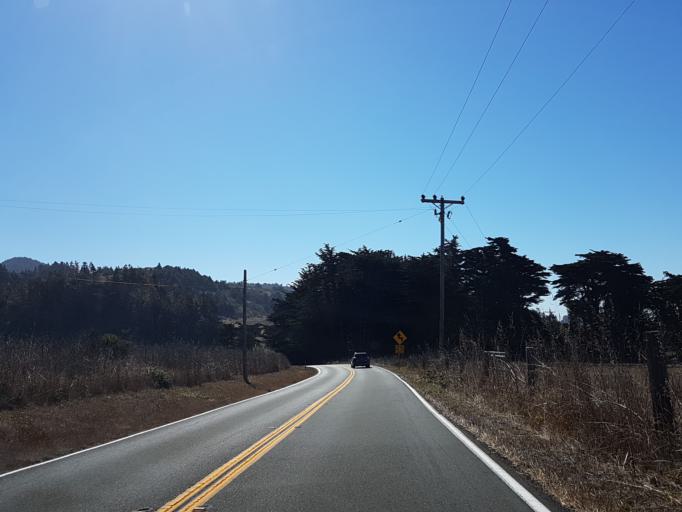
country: US
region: California
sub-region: Mendocino County
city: Boonville
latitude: 39.0536
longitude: -123.6850
